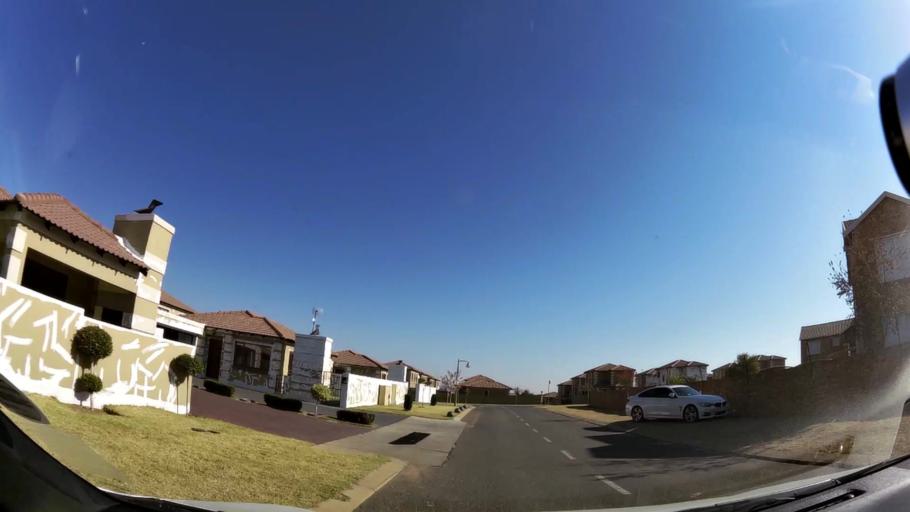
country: ZA
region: Gauteng
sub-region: City of Tshwane Metropolitan Municipality
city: Centurion
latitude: -25.9110
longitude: 28.1295
